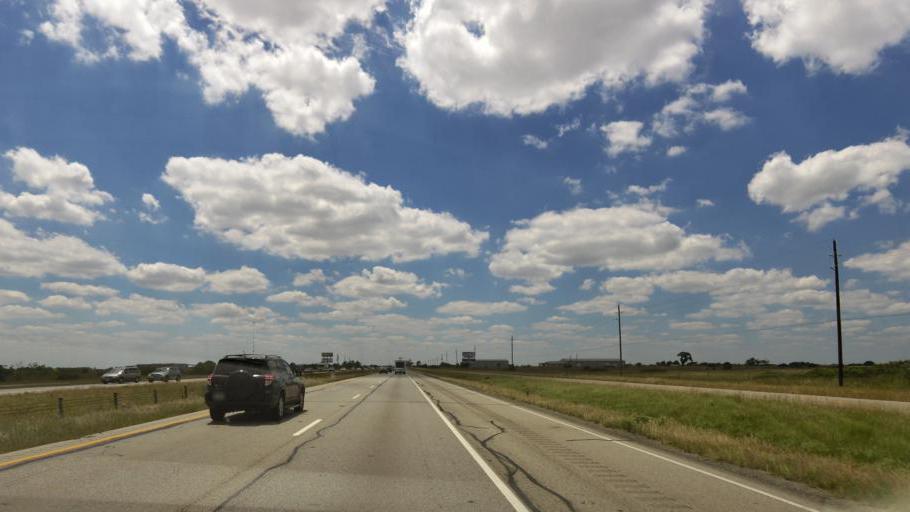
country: US
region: Texas
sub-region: Austin County
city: Sealy
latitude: 29.7550
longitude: -96.2502
